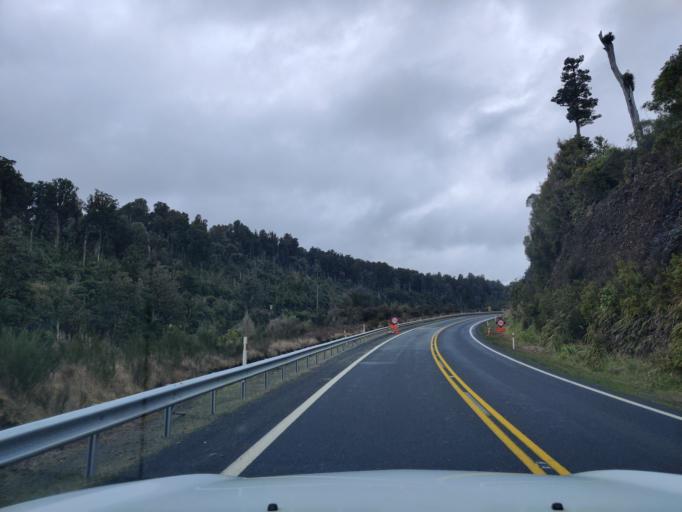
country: NZ
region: Manawatu-Wanganui
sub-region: Ruapehu District
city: Waiouru
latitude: -39.2651
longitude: 175.3941
